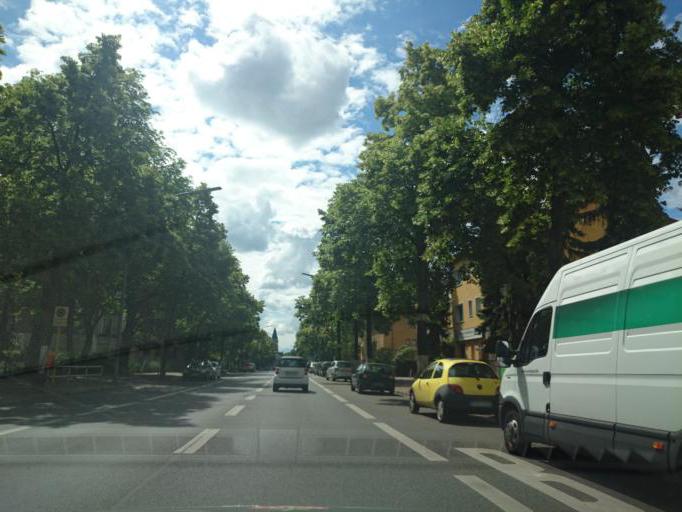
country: DE
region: Berlin
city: Lankwitz
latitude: 52.4420
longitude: 13.3416
